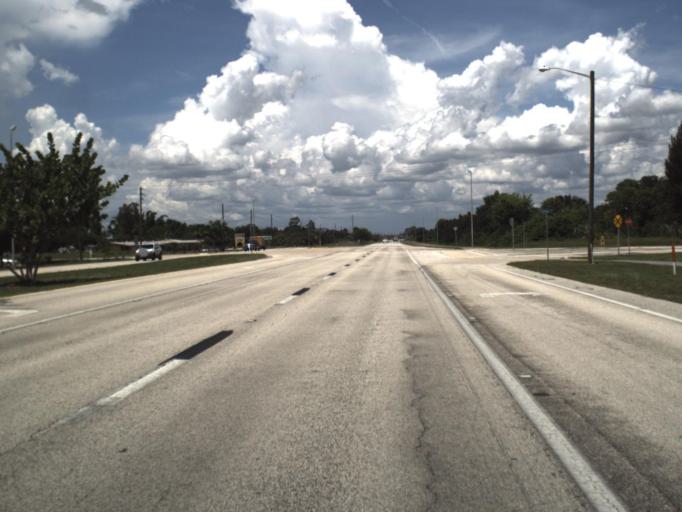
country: US
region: Florida
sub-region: Charlotte County
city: Charlotte Park
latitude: 26.8835
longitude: -82.0159
